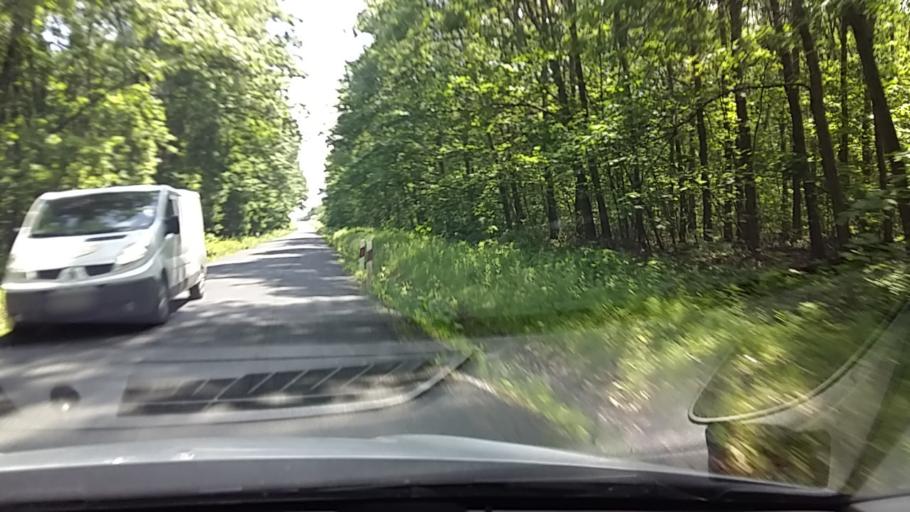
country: HU
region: Vas
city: Kormend
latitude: 46.9661
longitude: 16.5860
